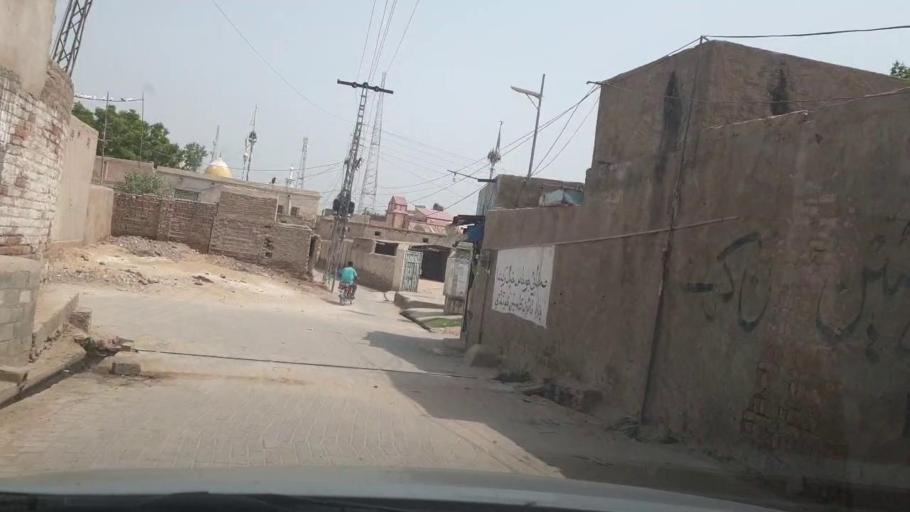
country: PK
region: Sindh
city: Kot Diji
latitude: 27.3391
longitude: 68.7079
